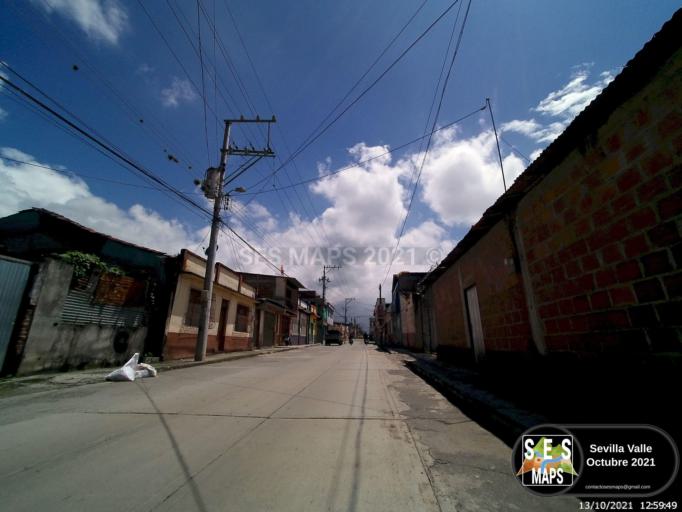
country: CO
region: Valle del Cauca
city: Sevilla
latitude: 4.2679
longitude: -75.9337
